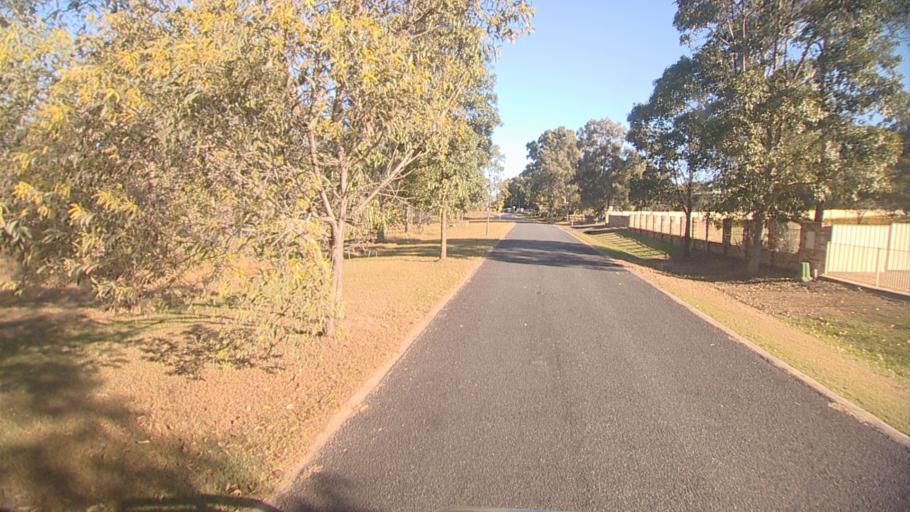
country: AU
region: Queensland
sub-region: Logan
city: North Maclean
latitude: -27.7349
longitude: 152.9708
